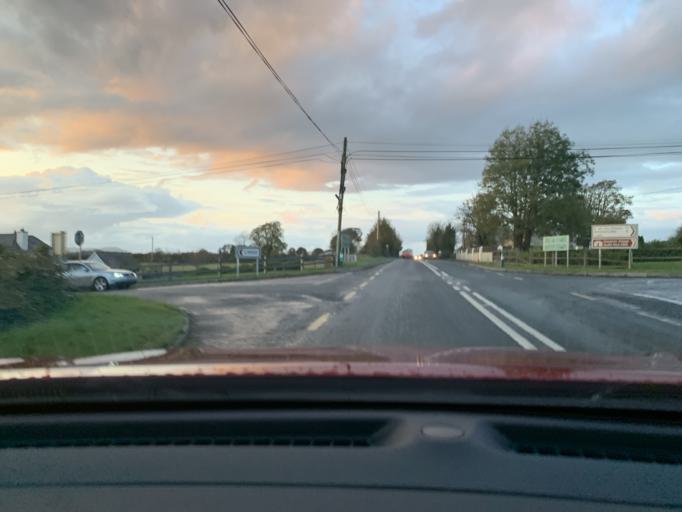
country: IE
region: Connaught
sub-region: Sligo
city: Collooney
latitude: 54.1314
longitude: -8.4444
